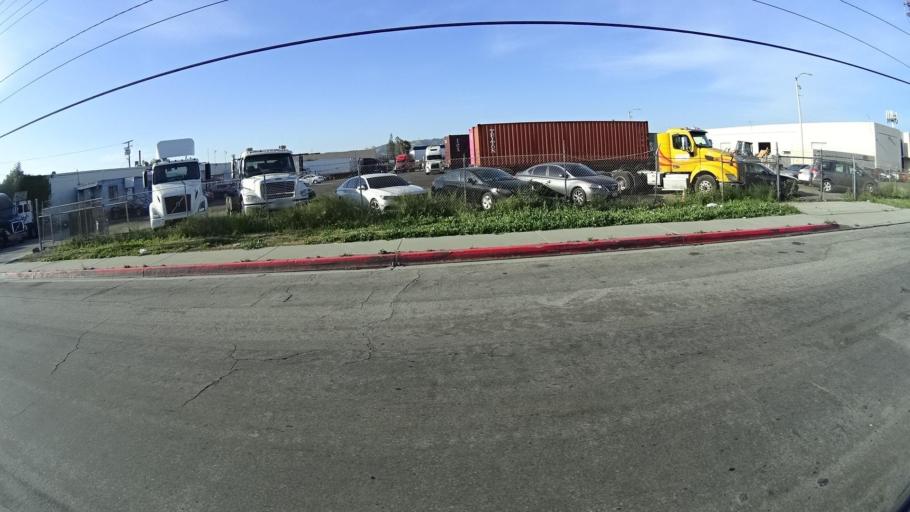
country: US
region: California
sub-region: Los Angeles County
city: South San Jose Hills
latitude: 33.9993
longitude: -117.8853
